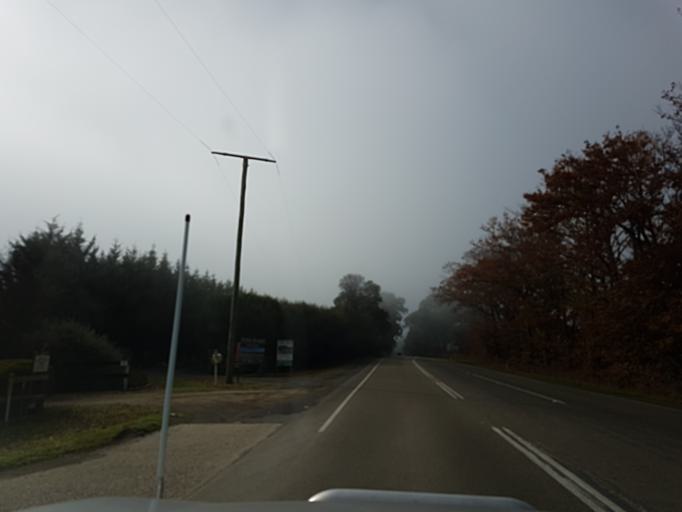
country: AU
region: Victoria
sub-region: Murrindindi
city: Kinglake West
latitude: -37.4189
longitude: 145.4277
